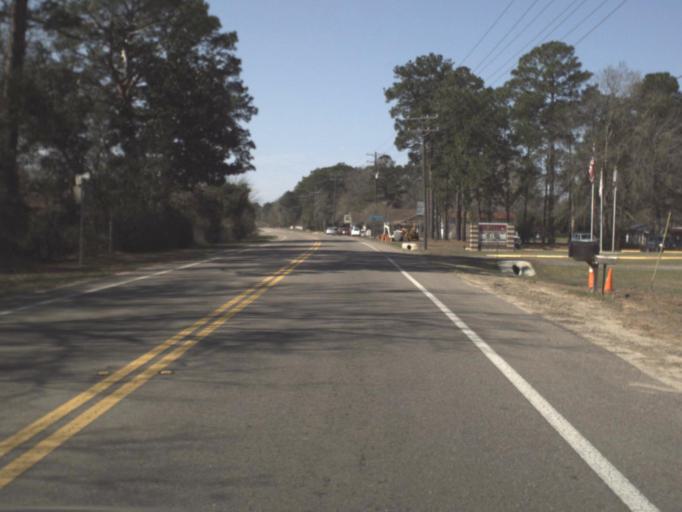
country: US
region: Florida
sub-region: Gadsden County
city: Gretna
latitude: 30.5930
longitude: -84.6657
